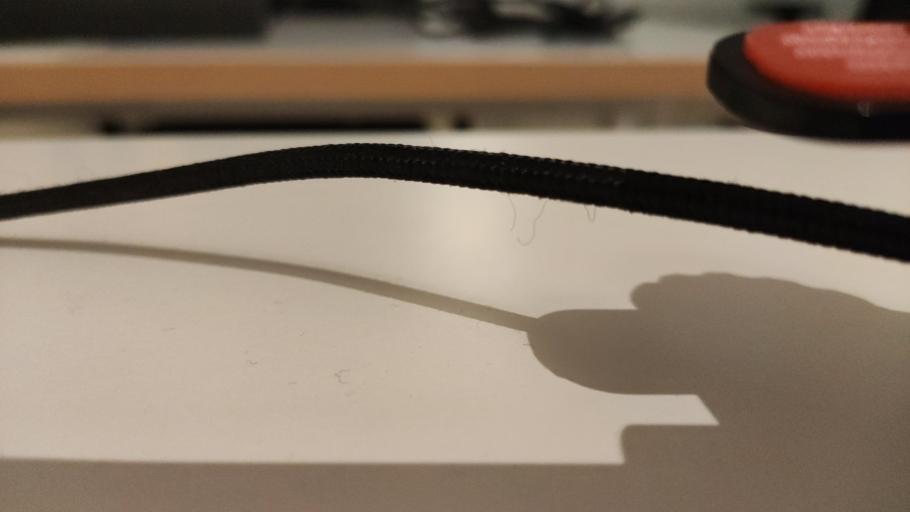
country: RU
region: Vladimir
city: Kirzhach
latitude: 56.0616
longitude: 38.7142
